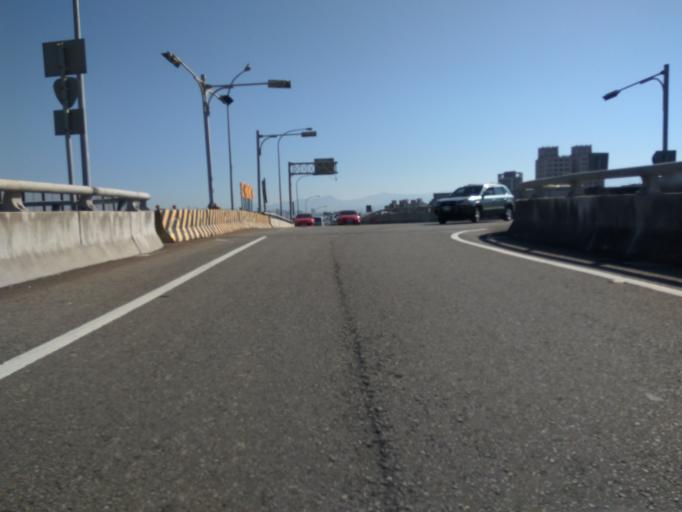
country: TW
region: Taiwan
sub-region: Hsinchu
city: Hsinchu
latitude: 24.8264
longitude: 120.9715
